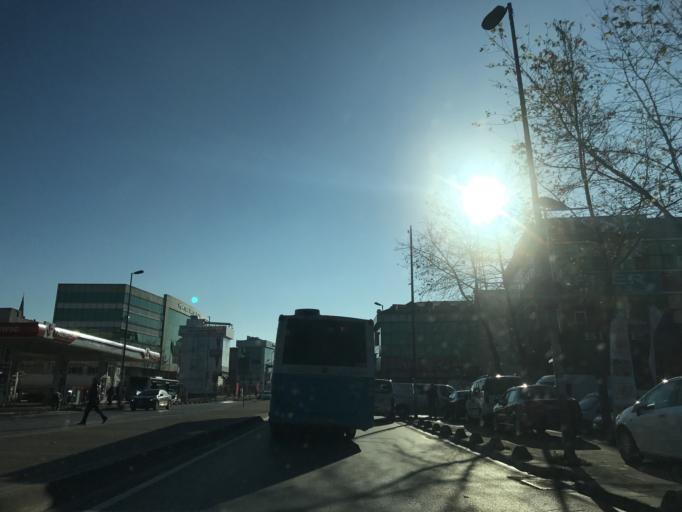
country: TR
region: Istanbul
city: Istanbul
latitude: 41.0419
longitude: 28.9191
